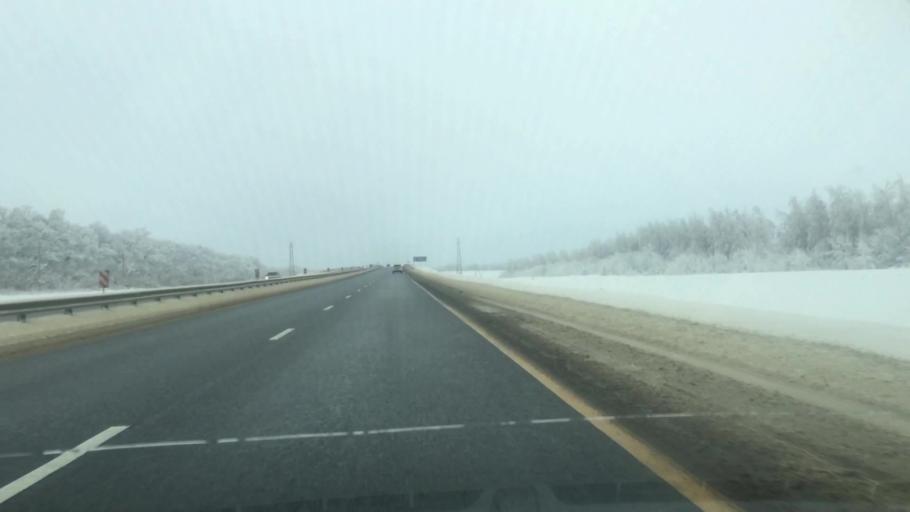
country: RU
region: Lipetsk
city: Zadonsk
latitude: 52.5096
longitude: 38.7557
